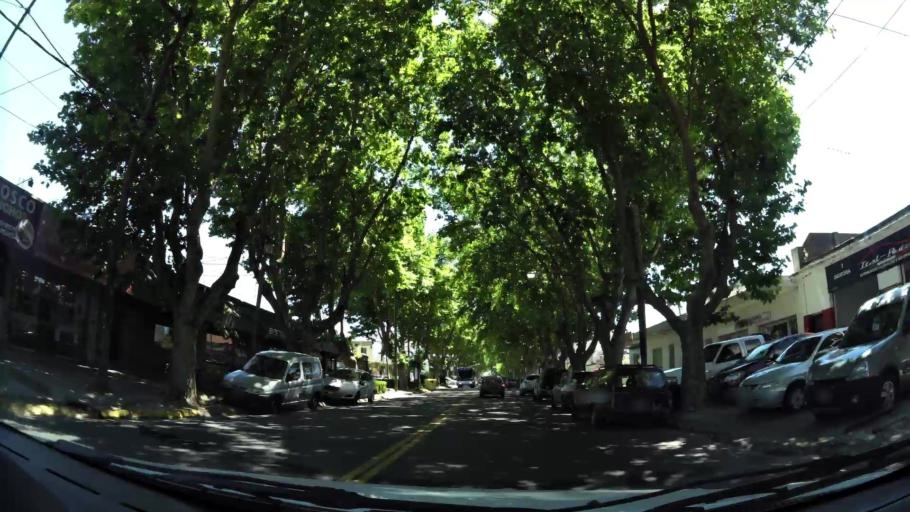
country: AR
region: Buenos Aires
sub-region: Partido de San Isidro
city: San Isidro
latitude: -34.5119
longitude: -58.5409
